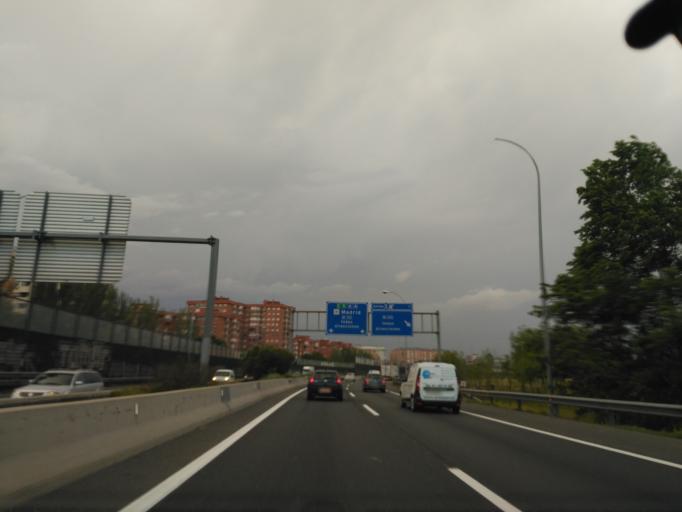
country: ES
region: Madrid
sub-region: Provincia de Madrid
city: Villaverde
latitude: 40.3534
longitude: -3.6774
